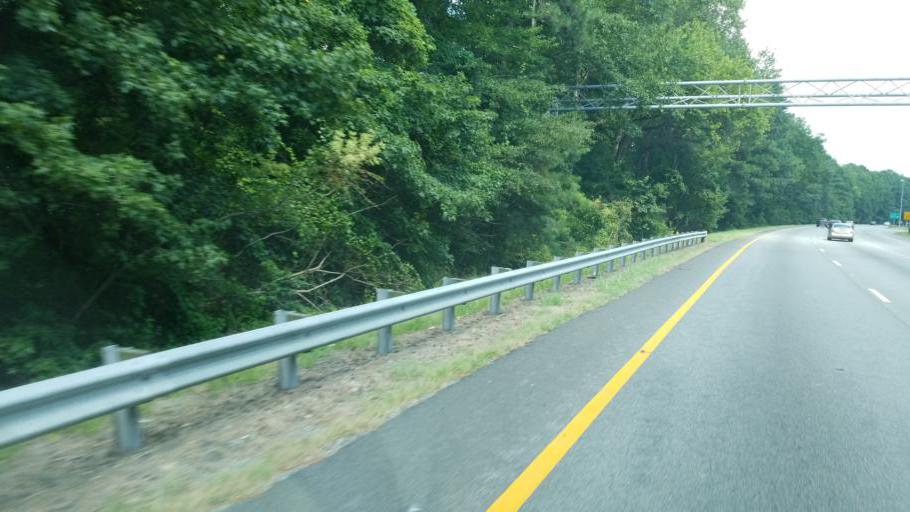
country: US
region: Virginia
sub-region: City of Portsmouth
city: Portsmouth Heights
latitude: 36.7757
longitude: -76.3725
